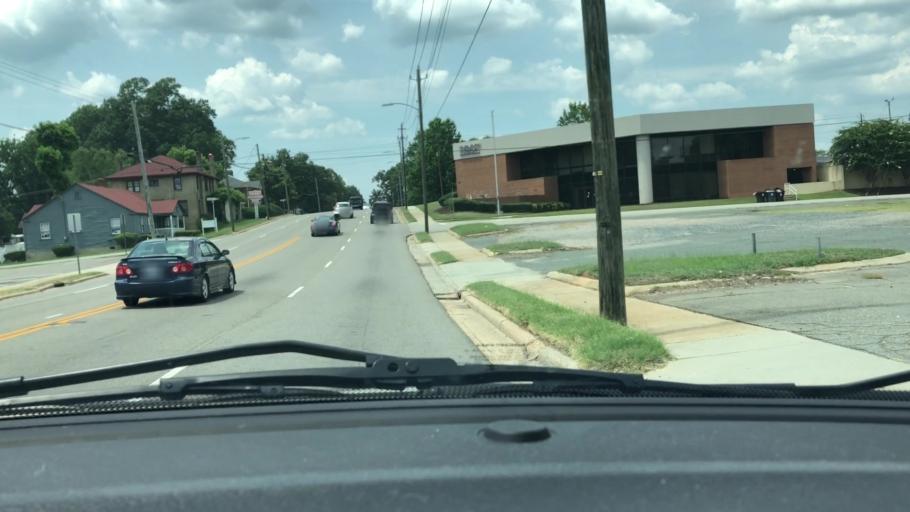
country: US
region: North Carolina
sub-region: Lee County
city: Sanford
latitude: 35.4807
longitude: -79.1811
